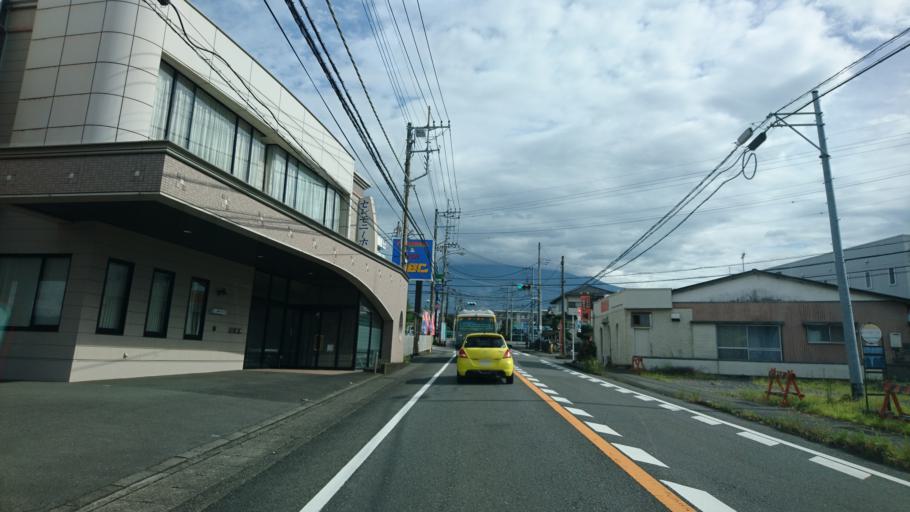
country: JP
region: Shizuoka
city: Fujinomiya
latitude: 35.2428
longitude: 138.6215
